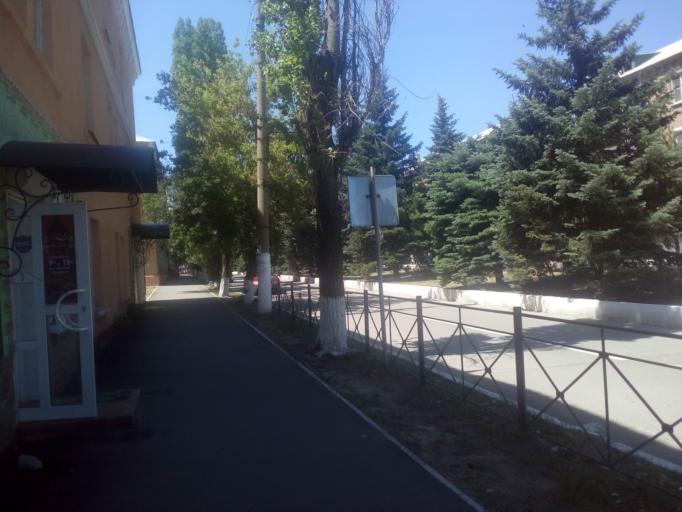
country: RU
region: Rostov
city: Sholokhovskiy
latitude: 48.2824
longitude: 41.0460
